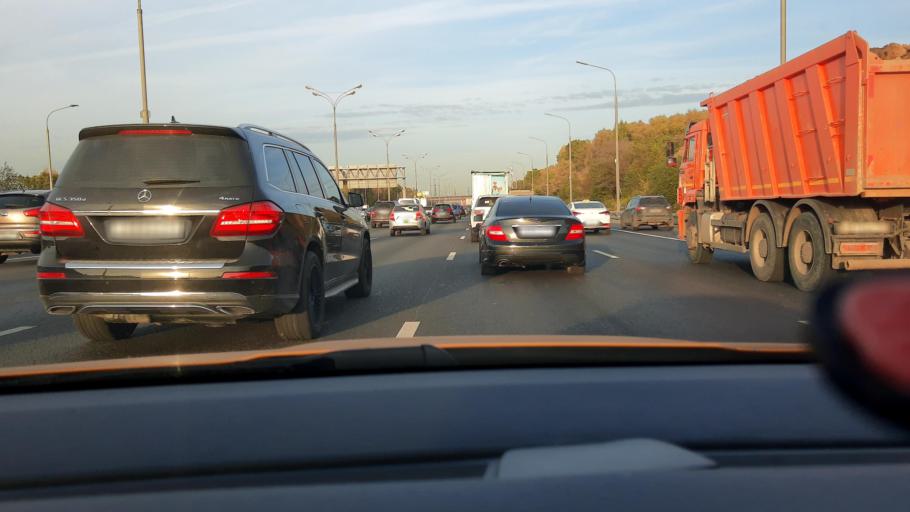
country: RU
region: Moscow
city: Businovo
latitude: 55.8973
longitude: 37.5093
